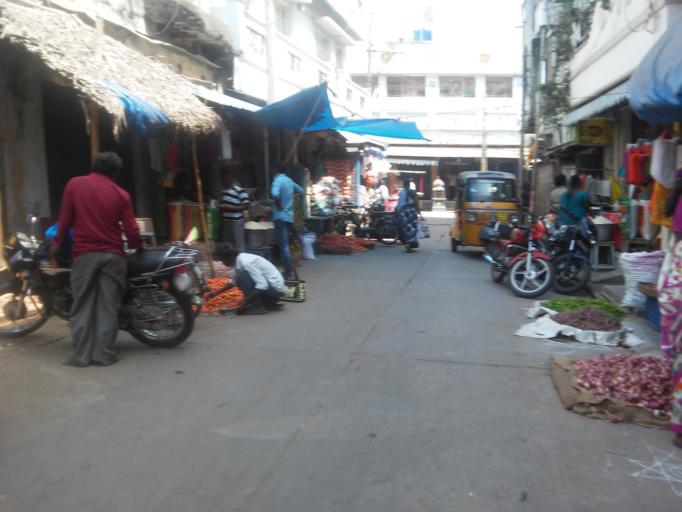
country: IN
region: Andhra Pradesh
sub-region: Chittoor
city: Chittoor
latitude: 13.2179
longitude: 79.0949
